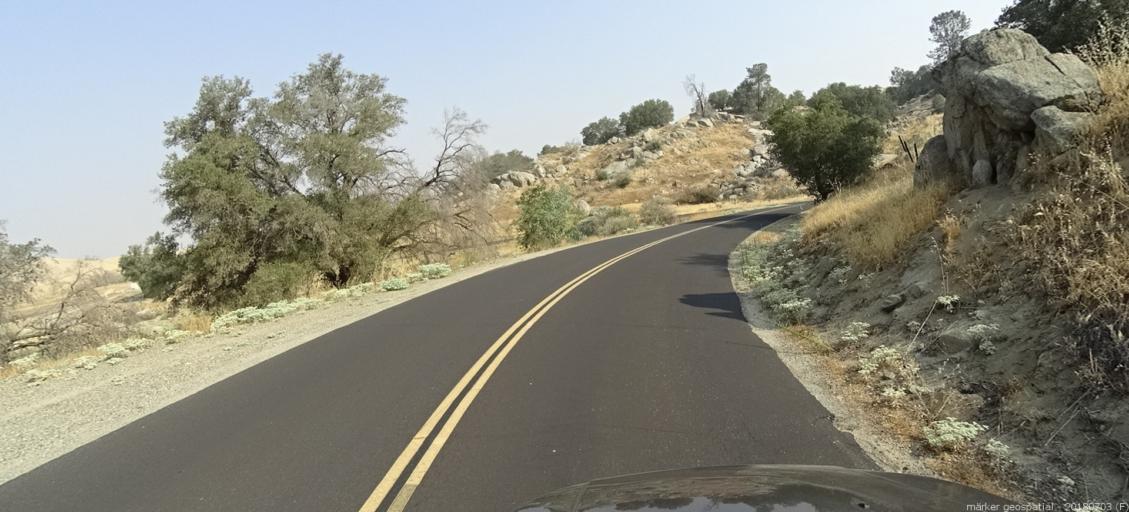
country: US
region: California
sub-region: Madera County
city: Bonadelle Ranchos-Madera Ranchos
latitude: 37.0176
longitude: -119.6902
